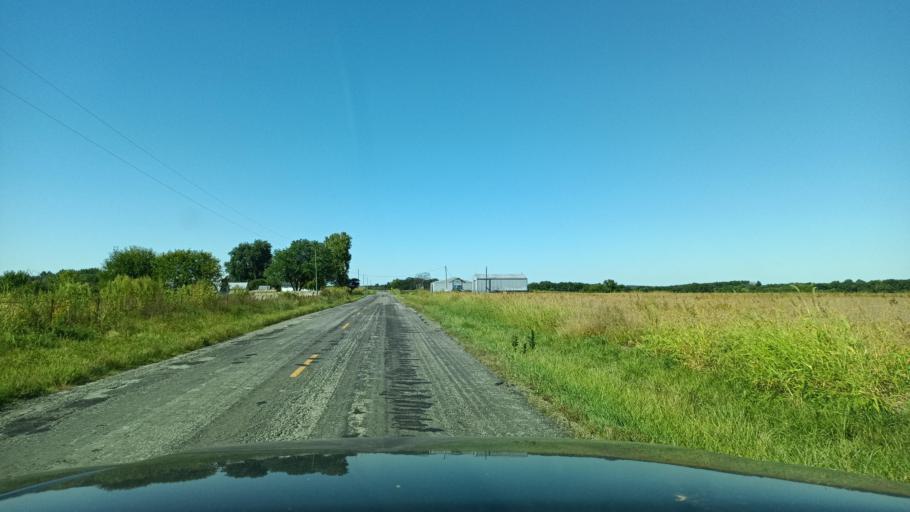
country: US
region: Missouri
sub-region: Scotland County
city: Memphis
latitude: 40.3548
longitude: -92.2272
